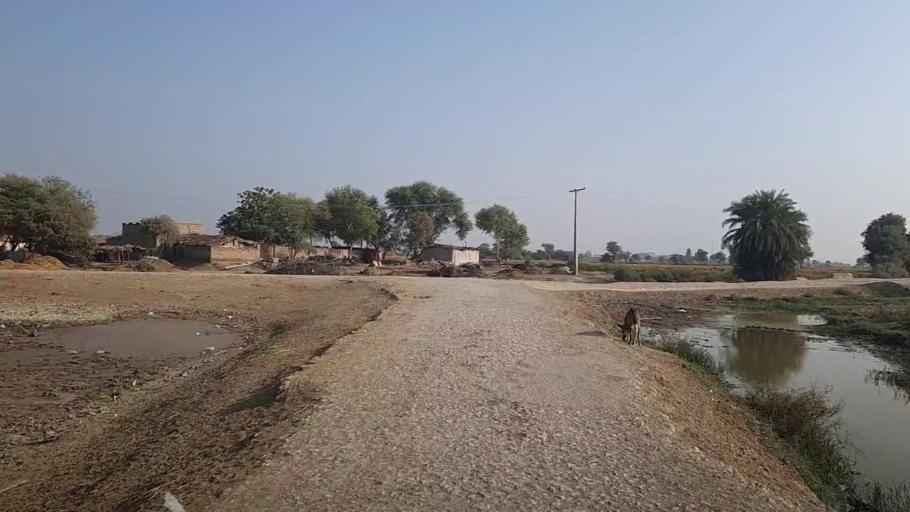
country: PK
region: Sindh
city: Kandhkot
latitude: 28.2873
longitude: 69.2579
